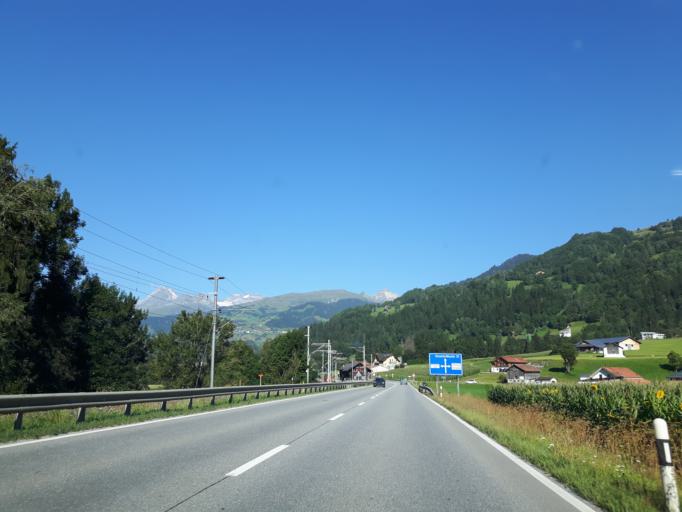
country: CH
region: Grisons
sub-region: Surselva District
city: Ilanz
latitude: 46.7737
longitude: 9.1805
